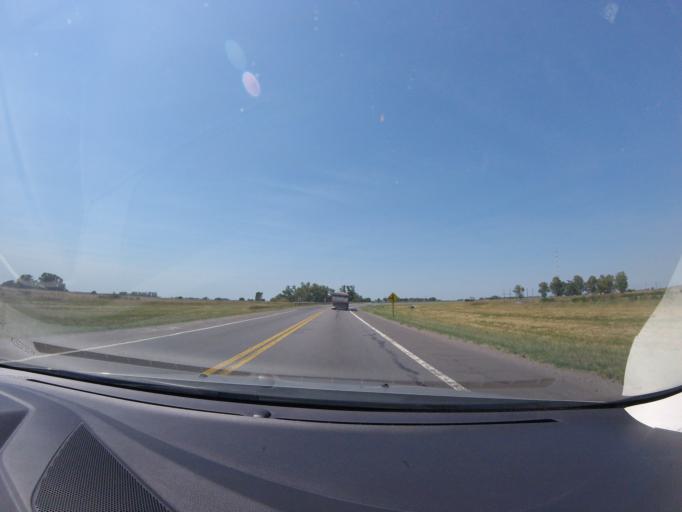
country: AR
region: Buenos Aires
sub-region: Partido de Las Flores
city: Las Flores
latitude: -35.8606
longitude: -58.9097
